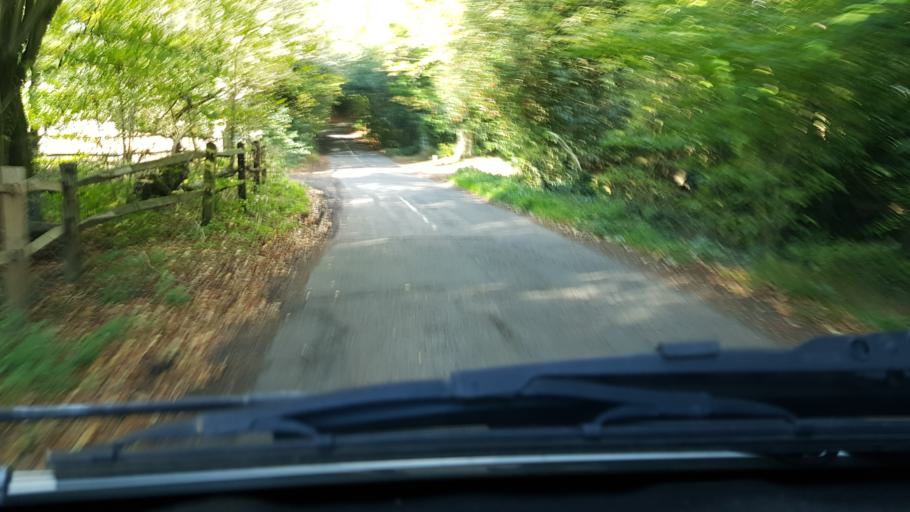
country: GB
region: England
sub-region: Surrey
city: Ockley
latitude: 51.1773
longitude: -0.3545
